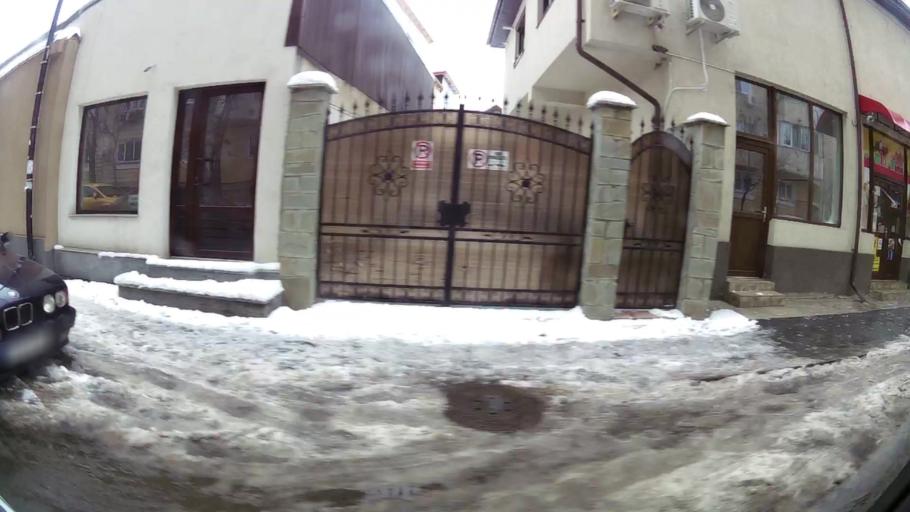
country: RO
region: Bucuresti
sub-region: Municipiul Bucuresti
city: Bucuresti
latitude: 44.3993
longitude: 26.1002
